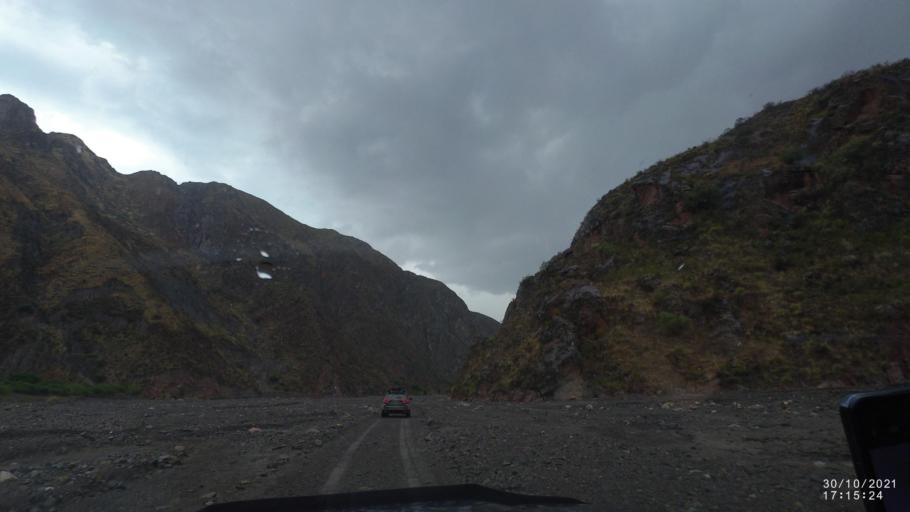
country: BO
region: Cochabamba
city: Colchani
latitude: -17.5439
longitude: -66.6274
